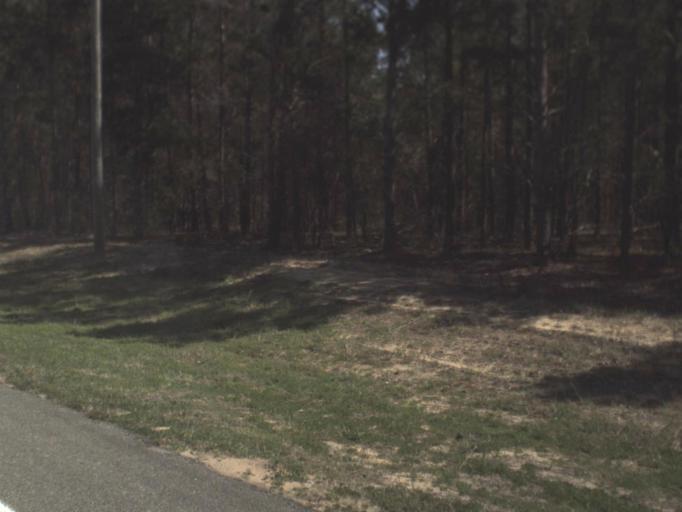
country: US
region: Florida
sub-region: Liberty County
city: Bristol
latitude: 30.4944
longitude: -84.8958
